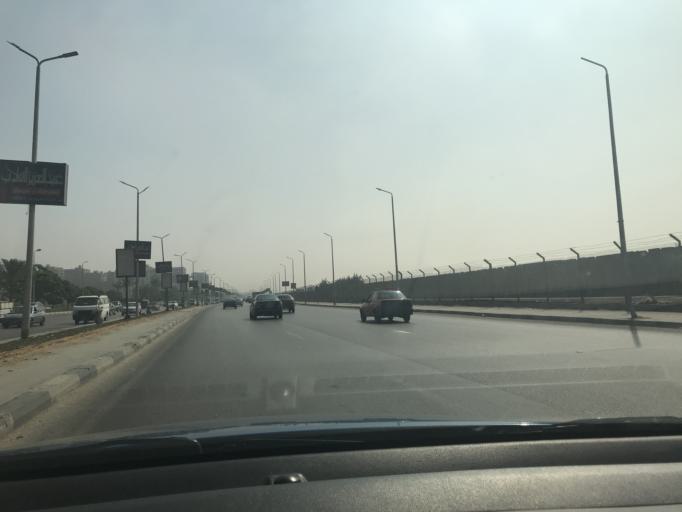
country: EG
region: Muhafazat al Qalyubiyah
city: Al Khankah
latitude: 30.1301
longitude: 31.3838
